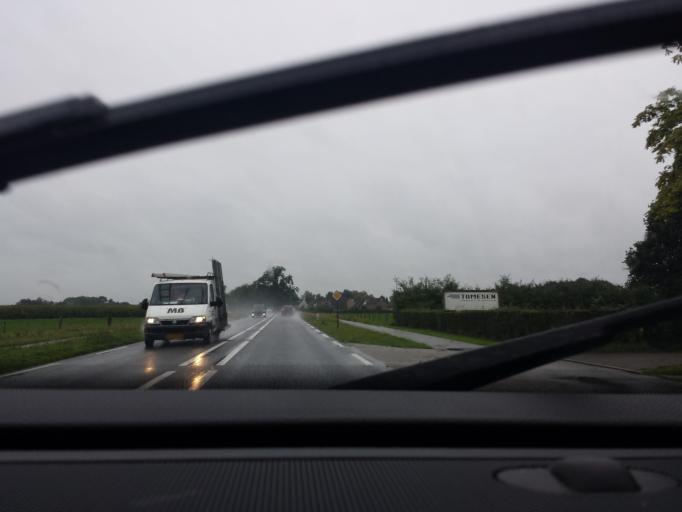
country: NL
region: Gelderland
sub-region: Gemeente Doetinchem
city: Doetinchem
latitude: 51.9280
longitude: 6.2709
